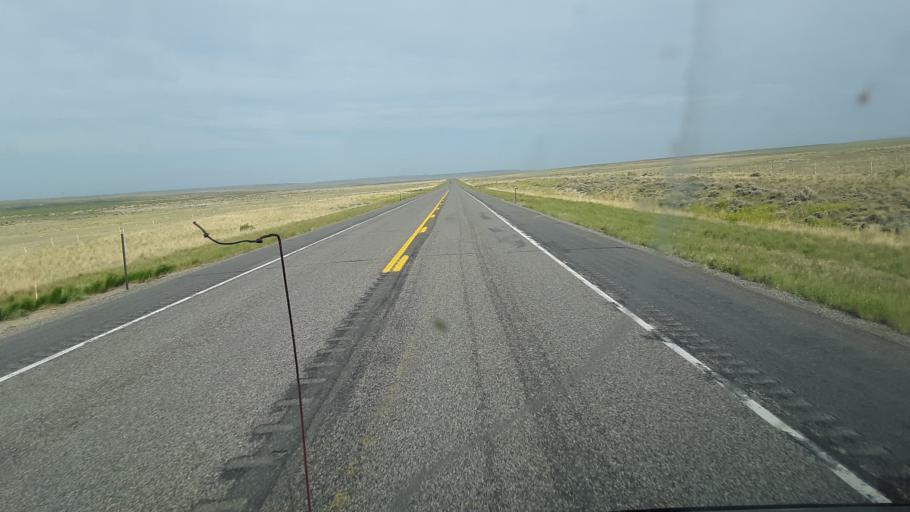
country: US
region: Wyoming
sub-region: Fremont County
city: Riverton
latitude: 43.1659
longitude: -107.7813
